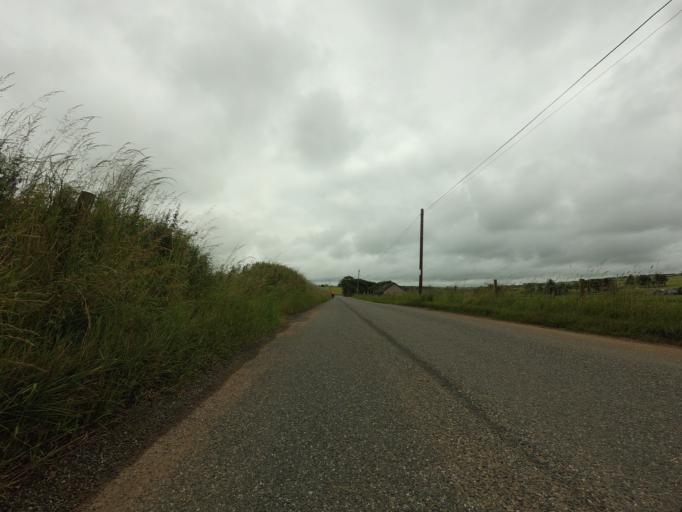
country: GB
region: Scotland
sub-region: Aberdeenshire
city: Turriff
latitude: 57.5401
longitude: -2.3688
